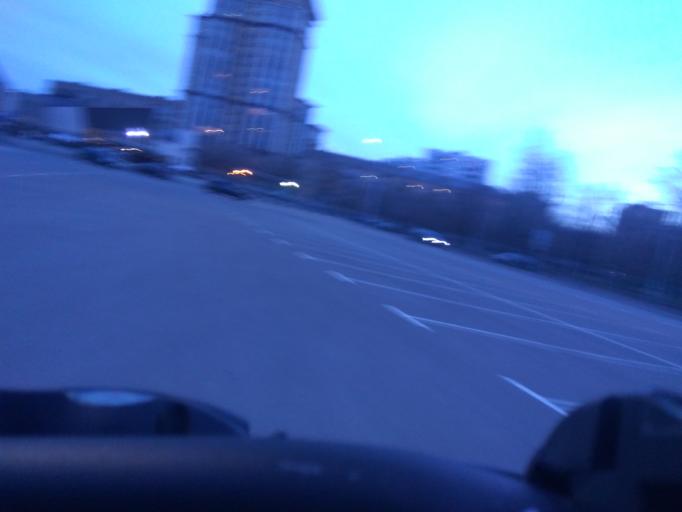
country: RU
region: Moskovskaya
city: Presnenskiy
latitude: 55.7438
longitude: 37.5539
